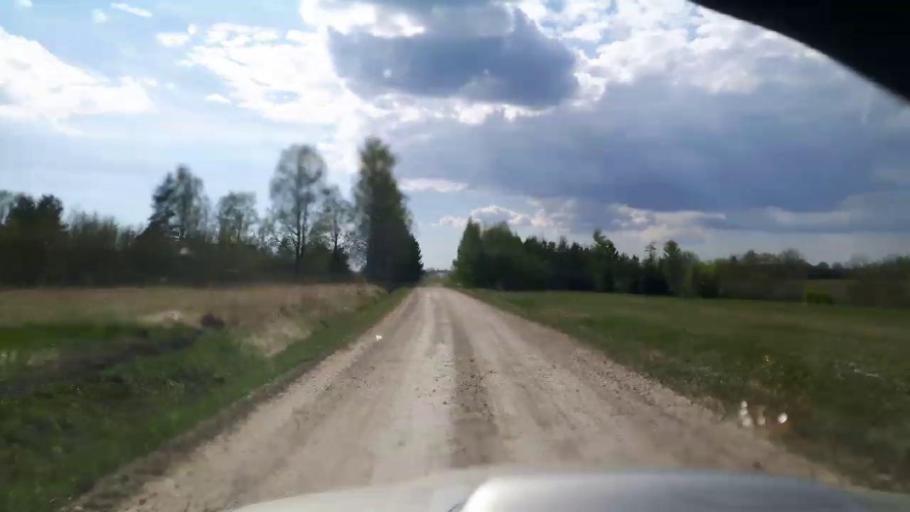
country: EE
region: Paernumaa
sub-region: Sindi linn
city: Sindi
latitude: 58.4229
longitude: 24.7449
